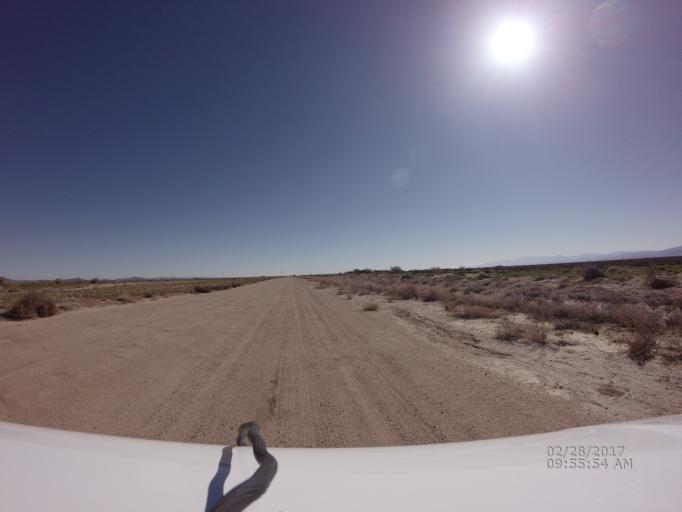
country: US
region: California
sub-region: Kern County
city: Rosamond
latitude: 34.8049
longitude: -118.3402
